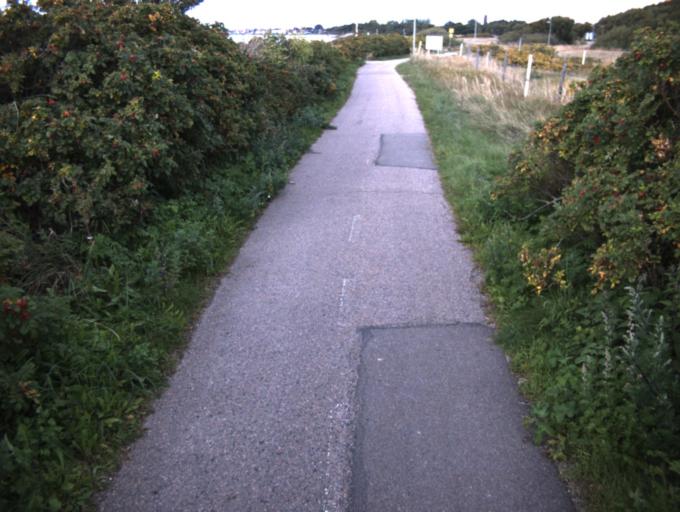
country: SE
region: Skane
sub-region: Helsingborg
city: Rydeback
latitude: 55.9799
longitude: 12.7544
